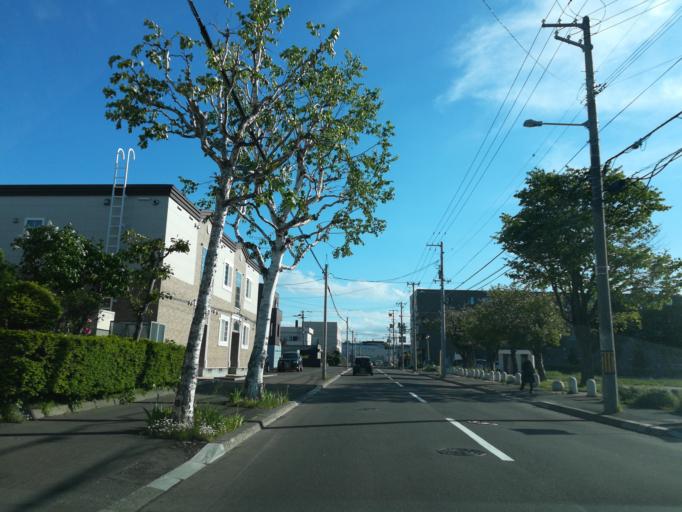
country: JP
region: Hokkaido
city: Sapporo
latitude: 43.0202
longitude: 141.4362
